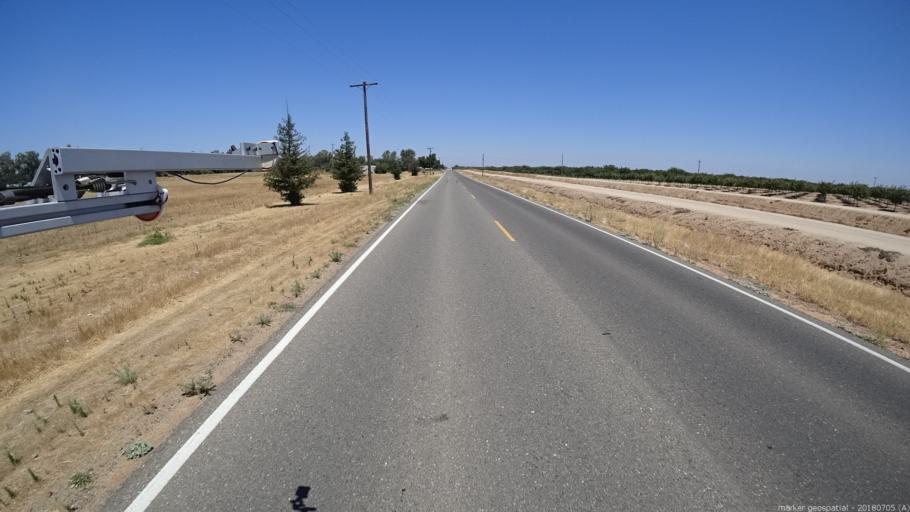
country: US
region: California
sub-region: Madera County
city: Madera Acres
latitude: 37.0389
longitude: -120.0745
